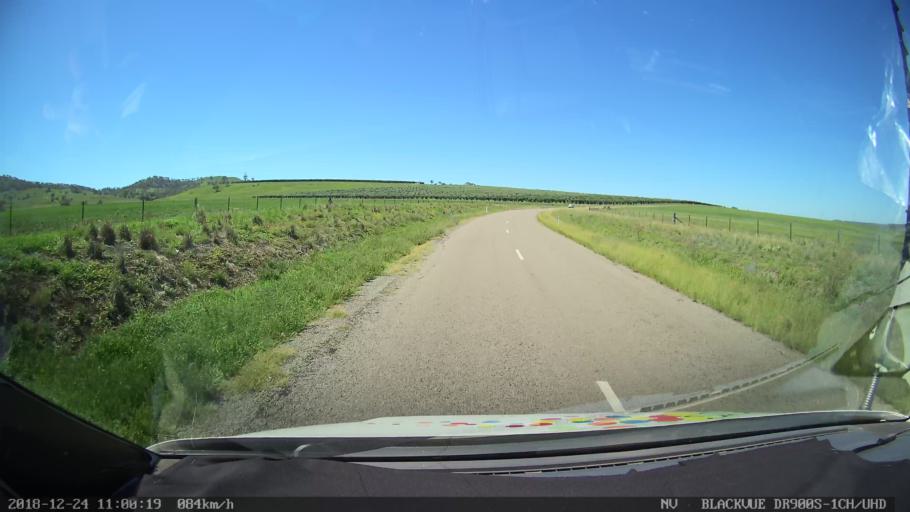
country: AU
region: New South Wales
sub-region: Upper Hunter Shire
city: Merriwa
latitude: -32.0662
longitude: 150.3941
